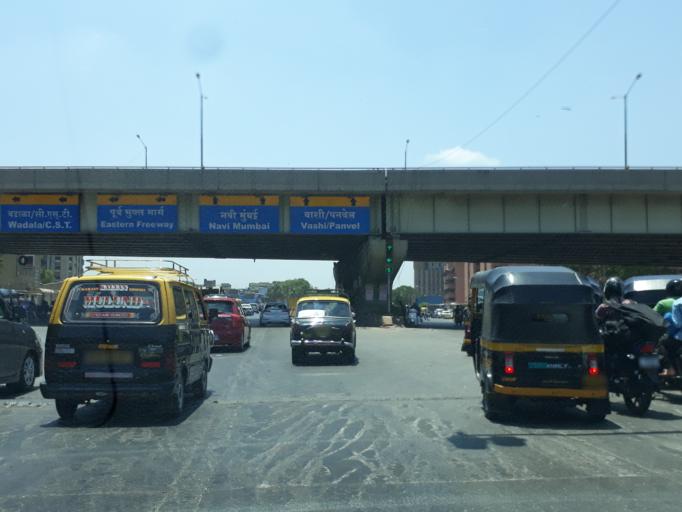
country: IN
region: Maharashtra
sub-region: Mumbai Suburban
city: Mumbai
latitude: 19.0634
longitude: 72.9142
